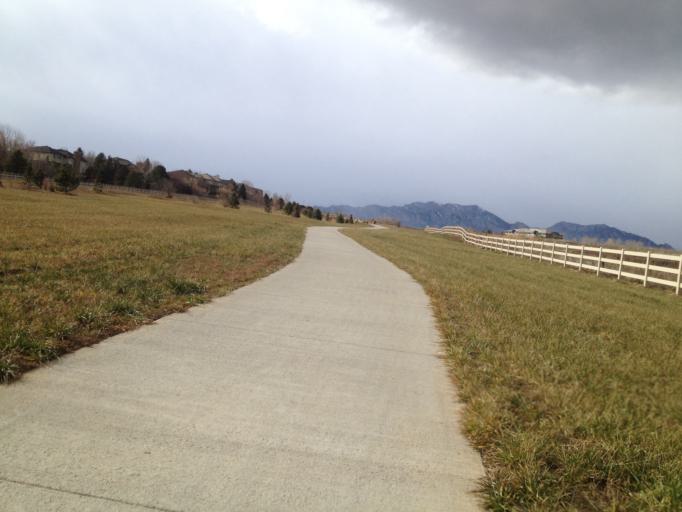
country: US
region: Colorado
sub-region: Boulder County
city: Superior
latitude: 39.9475
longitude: -105.1557
